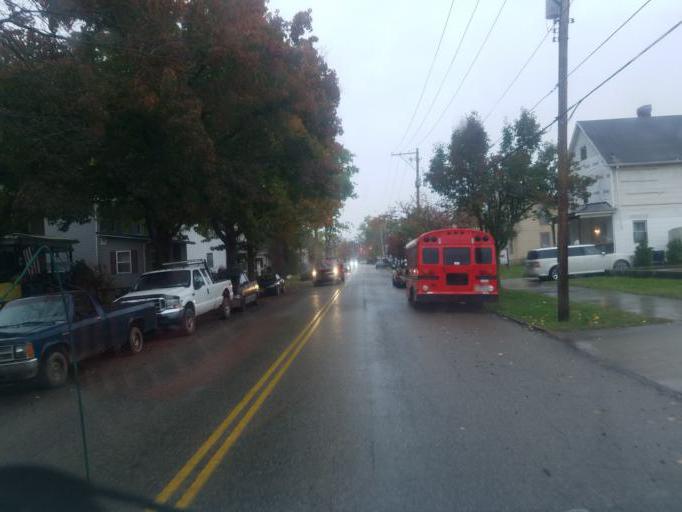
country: US
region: Ohio
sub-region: Washington County
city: Marietta
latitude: 39.4120
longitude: -81.4611
